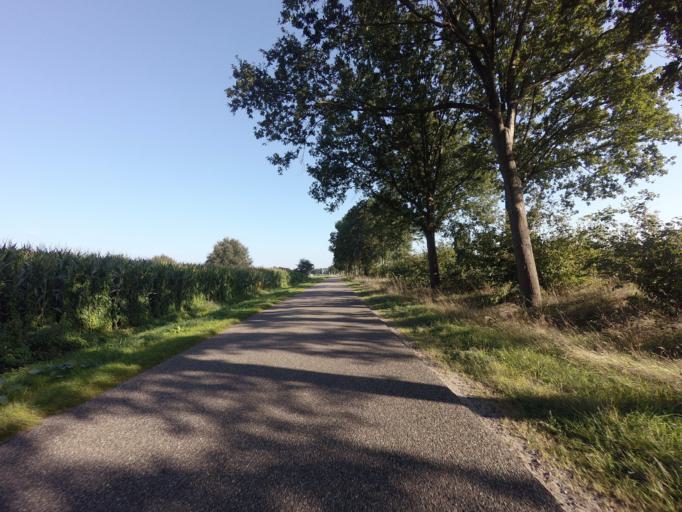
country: NL
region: Overijssel
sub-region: Gemeente Hardenberg
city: Hardenberg
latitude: 52.5506
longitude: 6.6554
